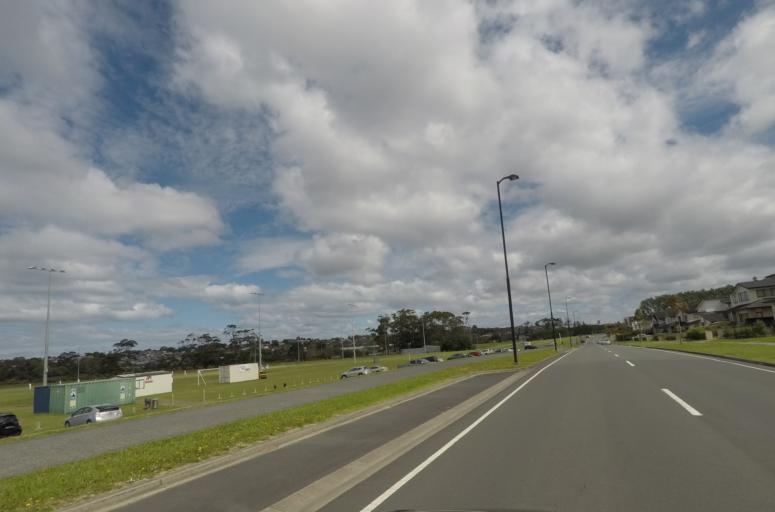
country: NZ
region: Auckland
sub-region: Auckland
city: Rothesay Bay
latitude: -36.6004
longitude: 174.6788
